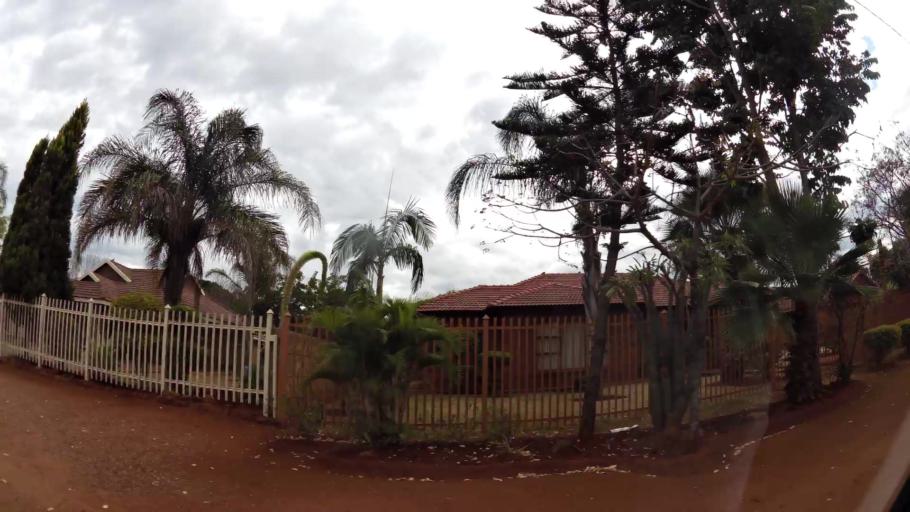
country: ZA
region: Limpopo
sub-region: Waterberg District Municipality
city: Modimolle
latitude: -24.5073
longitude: 28.7247
